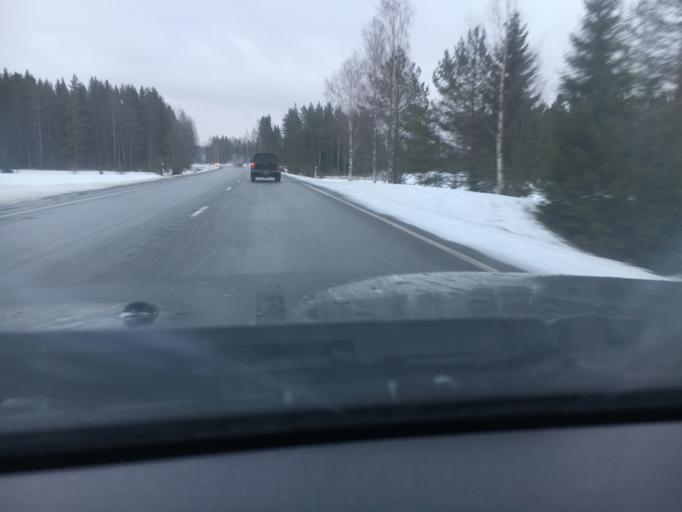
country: FI
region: Central Finland
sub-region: Jyvaeskylae
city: Toivakka
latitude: 62.2512
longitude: 26.2217
